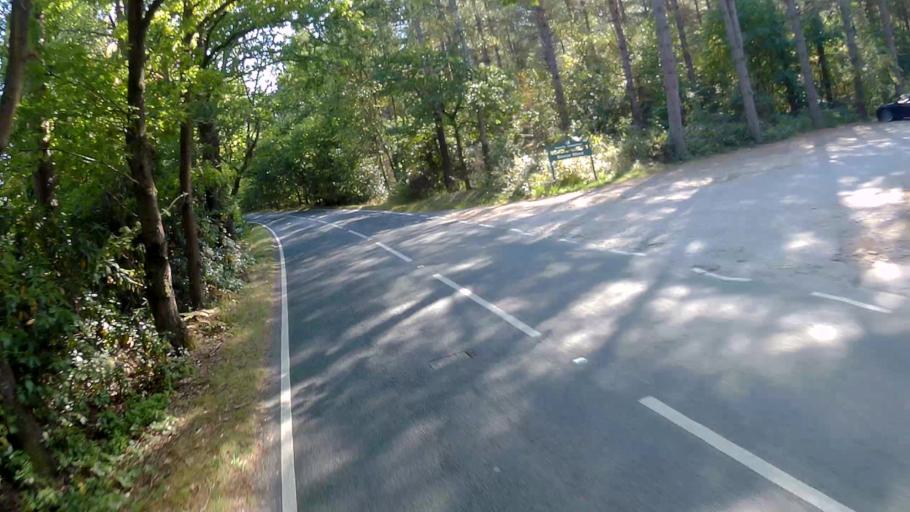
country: GB
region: England
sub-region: Surrey
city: Farnham
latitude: 51.1929
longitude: -0.7706
